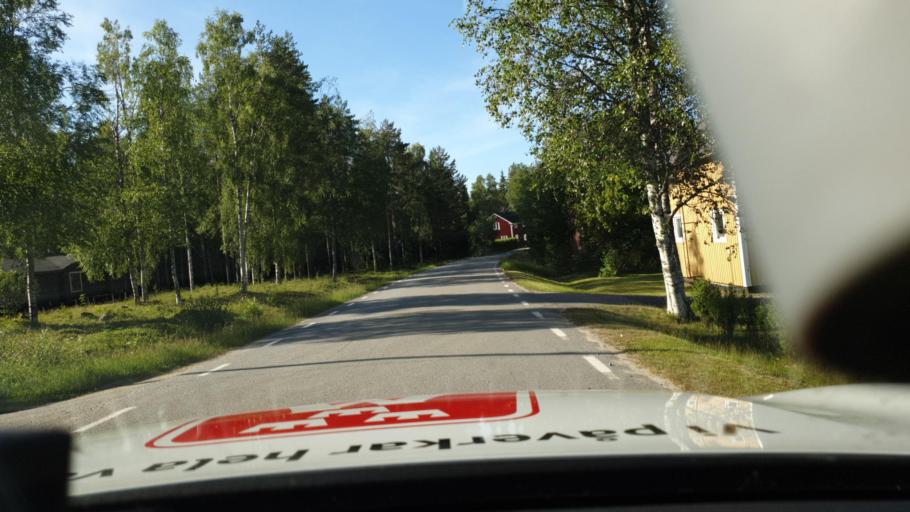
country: SE
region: Norrbotten
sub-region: Kalix Kommun
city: Toere
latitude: 65.8468
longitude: 22.6783
